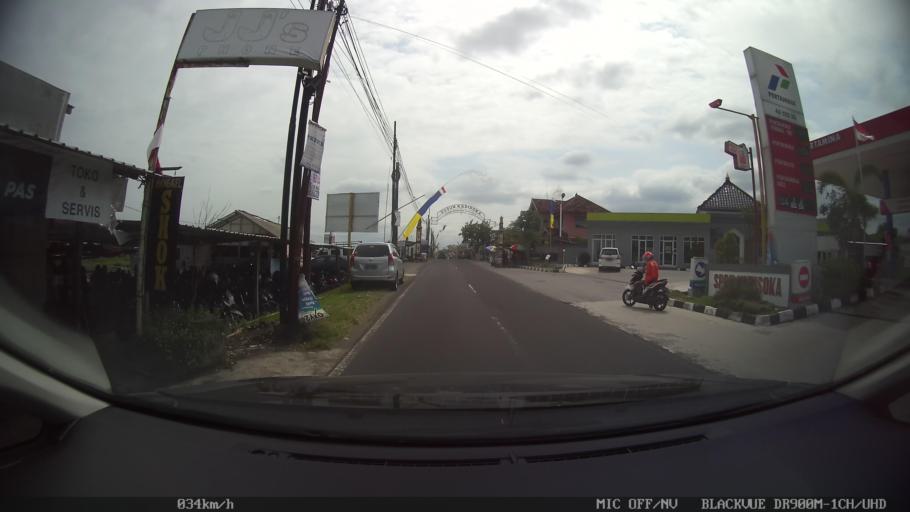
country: ID
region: Daerah Istimewa Yogyakarta
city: Depok
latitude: -7.7534
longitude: 110.4467
